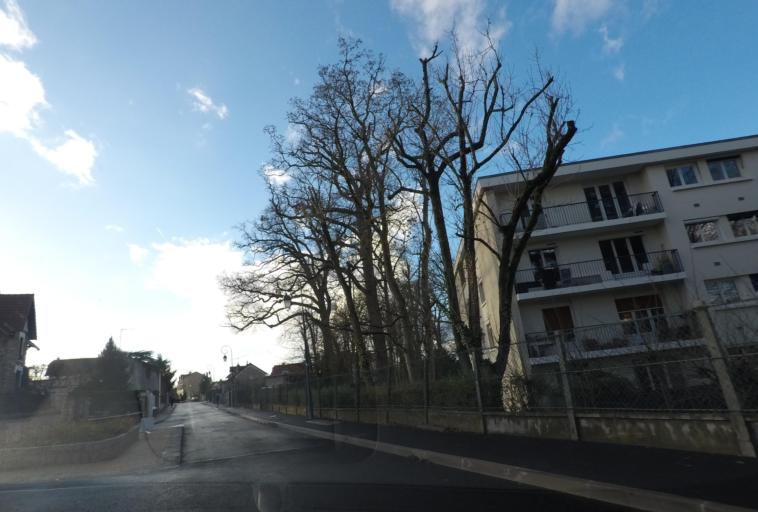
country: FR
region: Ile-de-France
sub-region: Departement de l'Essonne
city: Mennecy
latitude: 48.5704
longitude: 2.4356
